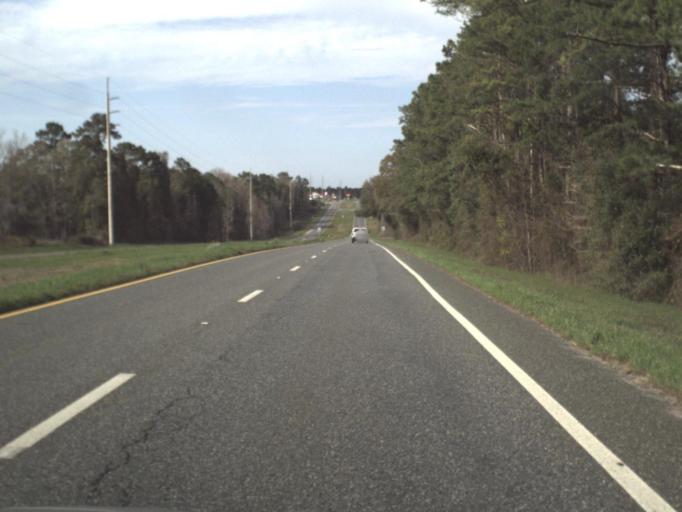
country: US
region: Florida
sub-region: Jefferson County
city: Monticello
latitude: 30.4622
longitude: -83.8922
